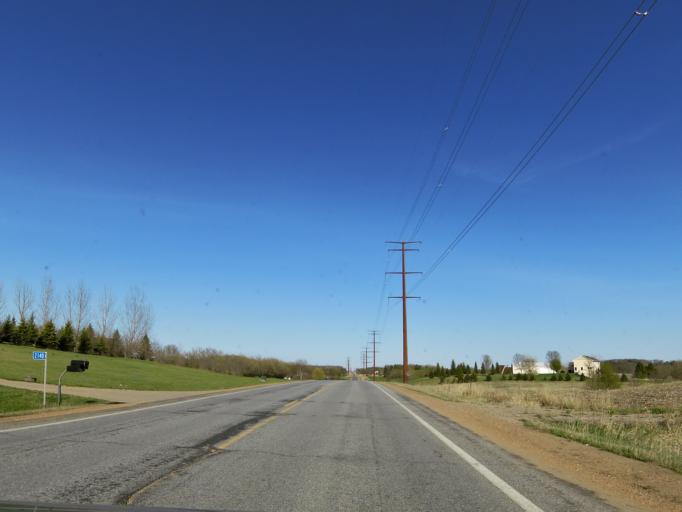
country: US
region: Minnesota
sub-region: Le Sueur County
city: New Prague
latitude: 44.5725
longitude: -93.4785
